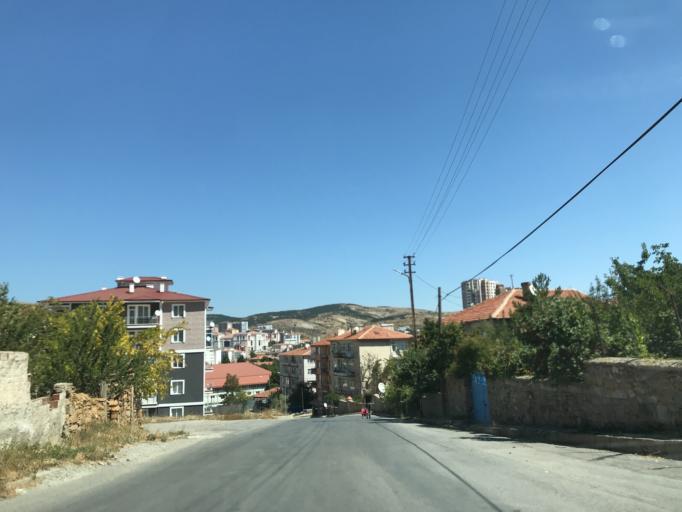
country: TR
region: Yozgat
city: Yozgat
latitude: 39.8190
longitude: 34.8176
